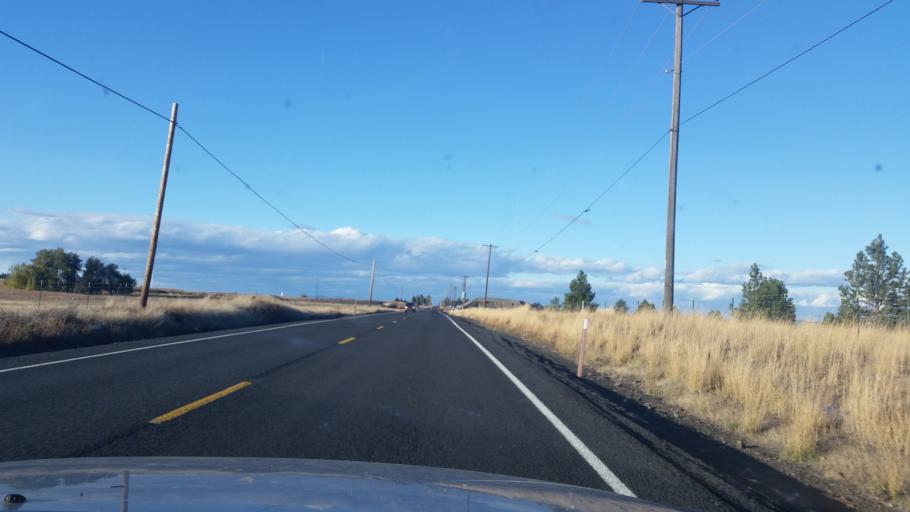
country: US
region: Washington
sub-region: Spokane County
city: Airway Heights
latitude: 47.6243
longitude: -117.6040
